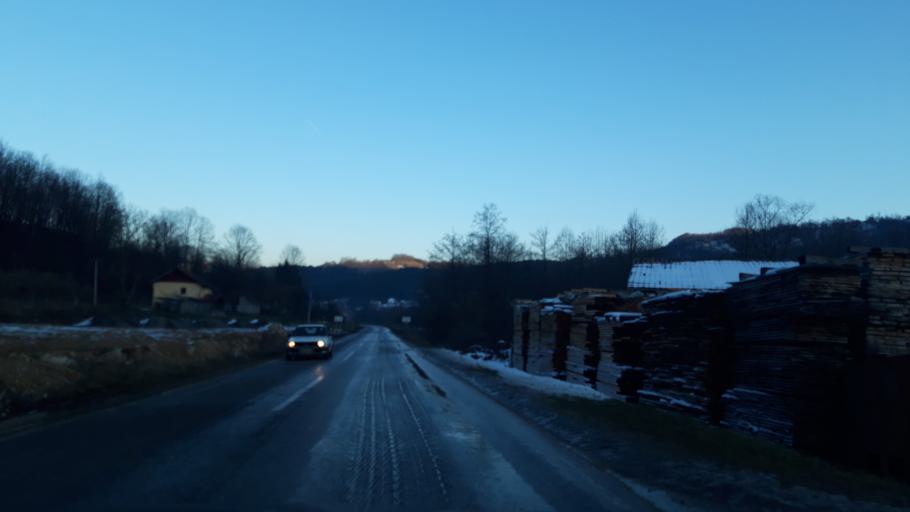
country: BA
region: Republika Srpska
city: Milici
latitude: 44.1639
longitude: 19.0600
